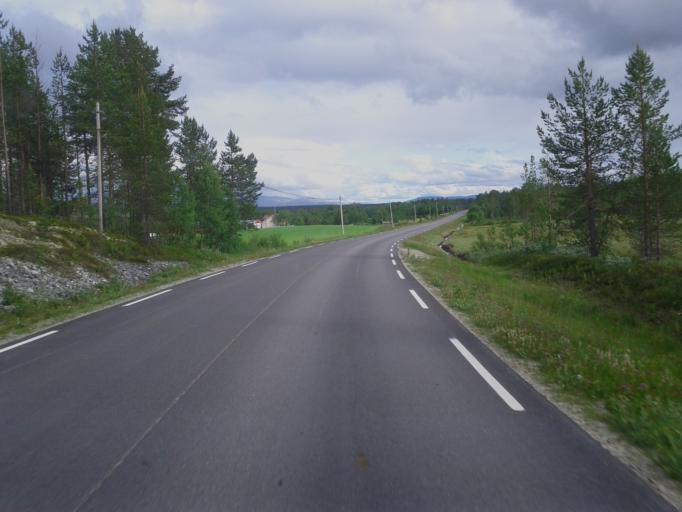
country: NO
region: Sor-Trondelag
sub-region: Roros
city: Roros
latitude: 62.3028
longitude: 11.7187
